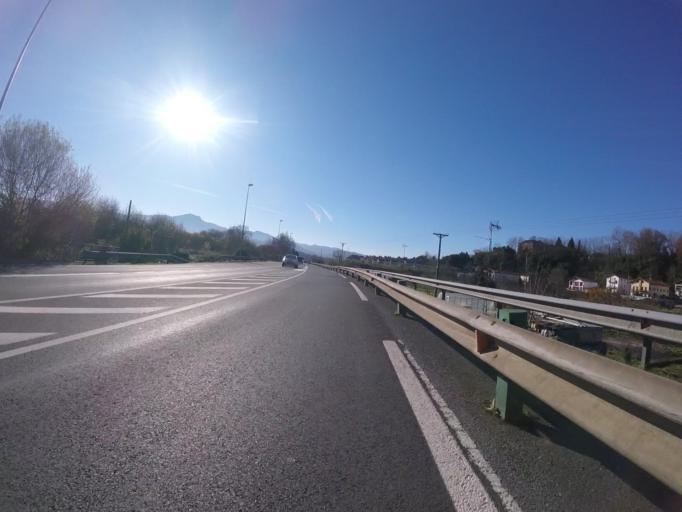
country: ES
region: Basque Country
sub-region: Provincia de Guipuzcoa
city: Fuenterrabia
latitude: 43.3559
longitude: -1.7955
